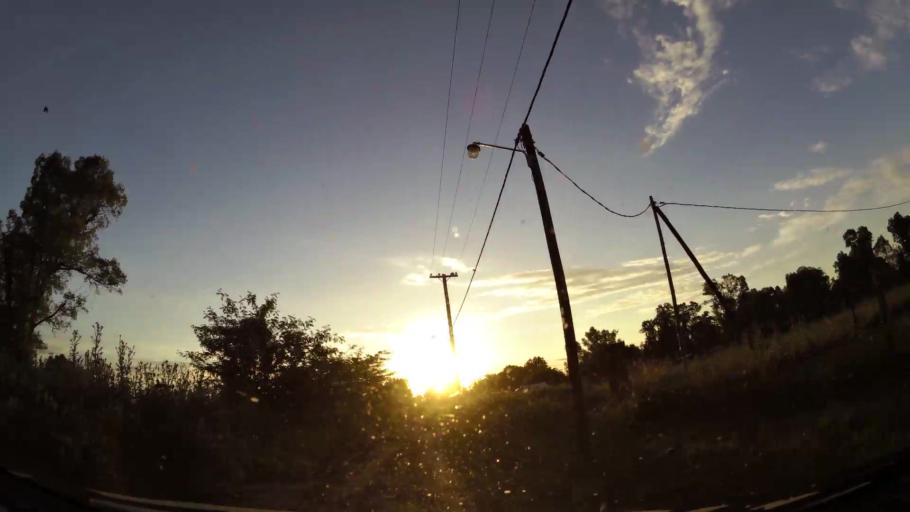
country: AR
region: Buenos Aires
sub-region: Partido de Merlo
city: Merlo
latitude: -34.6690
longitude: -58.7800
